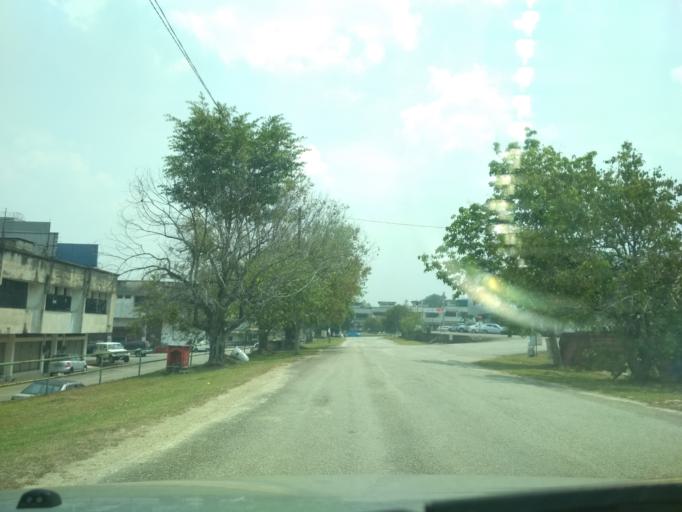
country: MY
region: Kedah
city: Kulim
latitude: 5.3546
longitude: 100.5324
